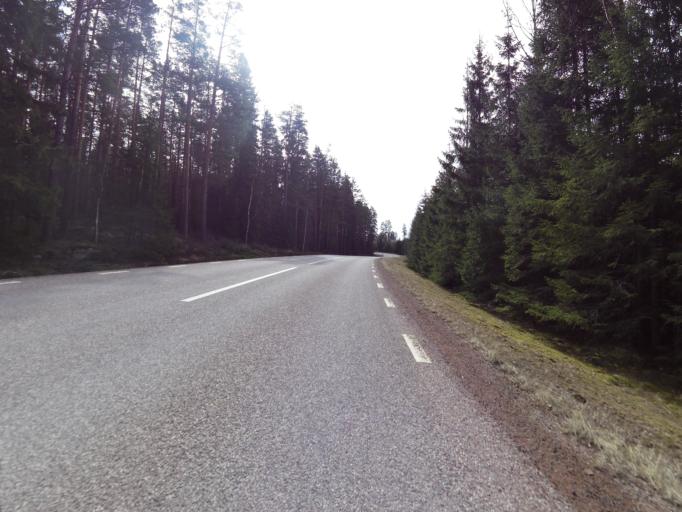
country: SE
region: Dalarna
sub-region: Hedemora Kommun
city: Langshyttan
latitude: 60.5284
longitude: 16.1330
